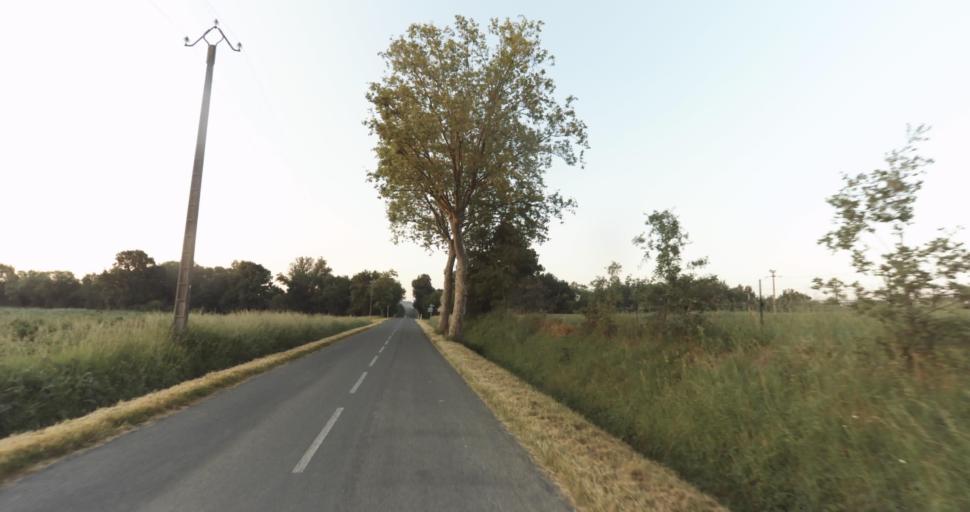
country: FR
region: Midi-Pyrenees
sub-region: Departement du Gers
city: Pujaudran
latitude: 43.6490
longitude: 1.1365
